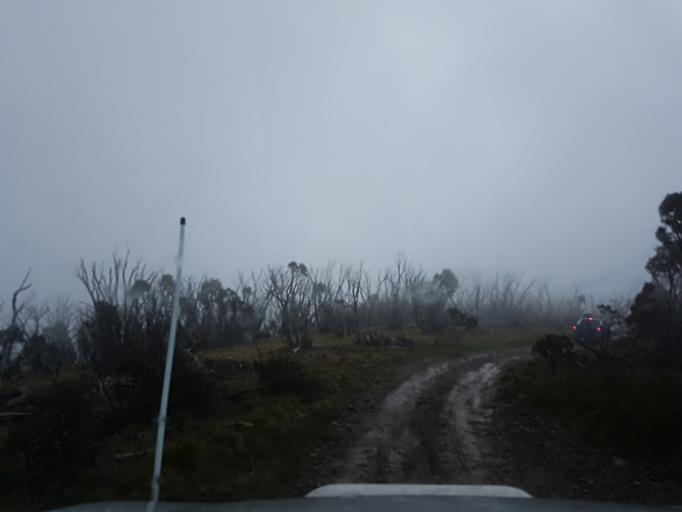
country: AU
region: Victoria
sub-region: Alpine
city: Mount Beauty
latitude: -37.0893
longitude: 147.0730
